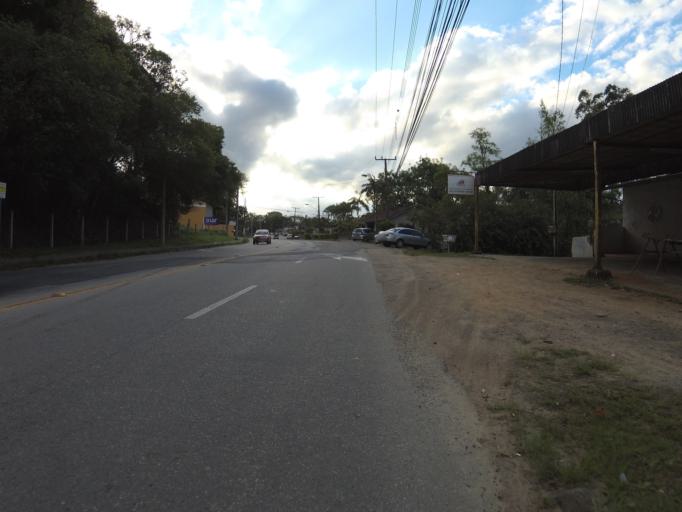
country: BR
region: Santa Catarina
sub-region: Blumenau
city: Blumenau
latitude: -26.8867
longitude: -49.1154
